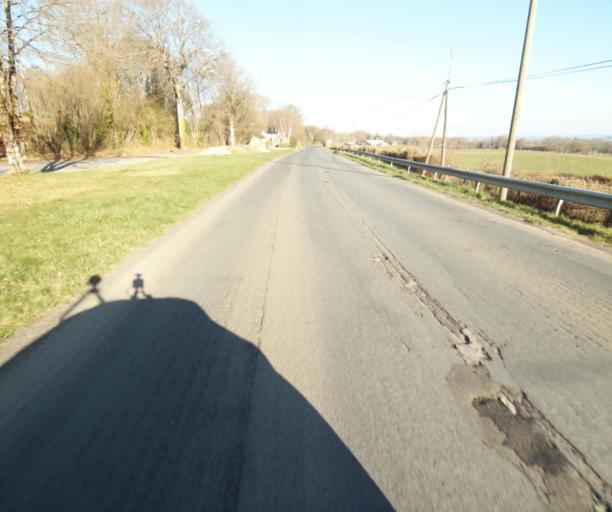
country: FR
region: Limousin
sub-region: Departement de la Correze
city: Uzerche
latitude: 45.3888
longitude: 1.5991
